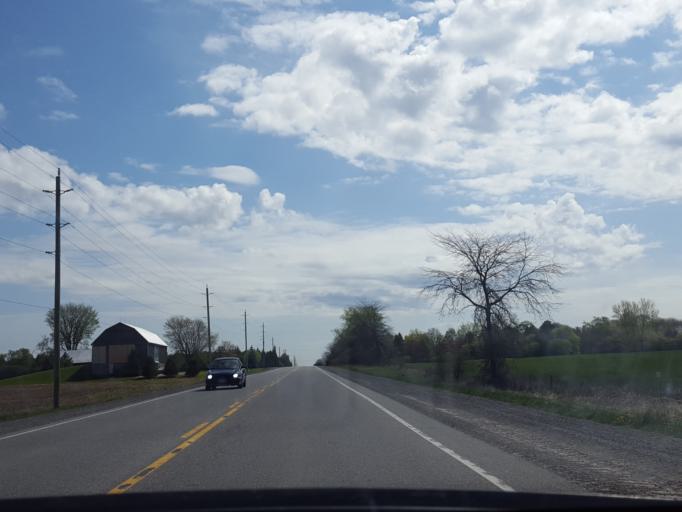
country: CA
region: Ontario
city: Oshawa
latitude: 44.1124
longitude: -78.8534
